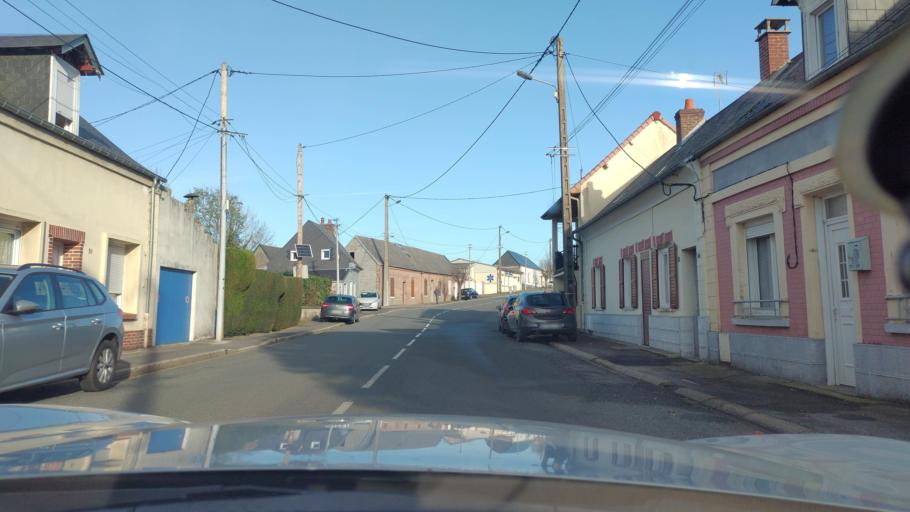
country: FR
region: Picardie
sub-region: Departement de la Somme
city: Fressenneville
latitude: 50.0718
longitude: 1.5830
